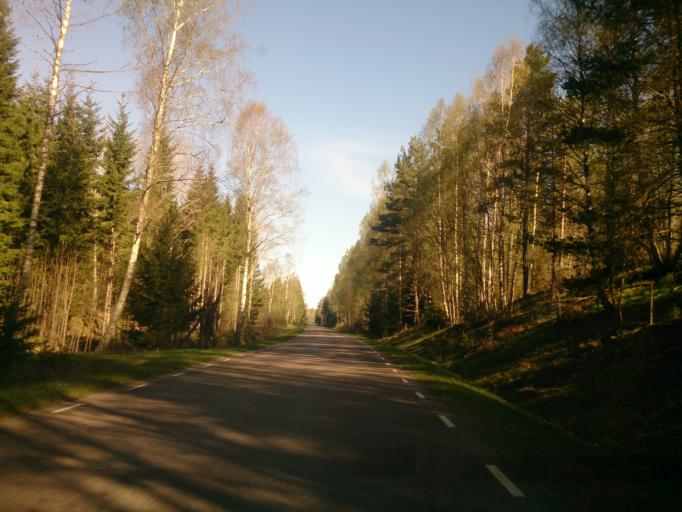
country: SE
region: OEstergoetland
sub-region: Linkopings Kommun
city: Ljungsbro
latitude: 58.5984
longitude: 15.4937
